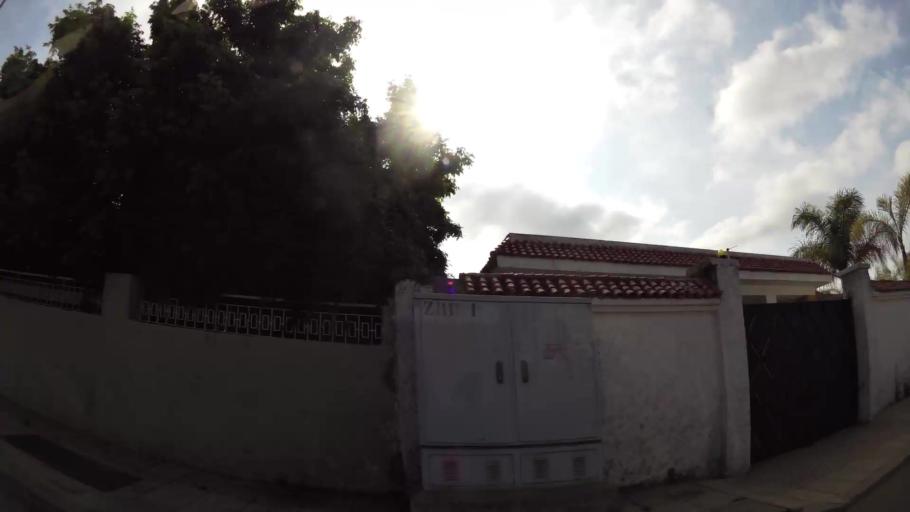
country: MA
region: Rabat-Sale-Zemmour-Zaer
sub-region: Rabat
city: Rabat
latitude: 33.9643
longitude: -6.8375
